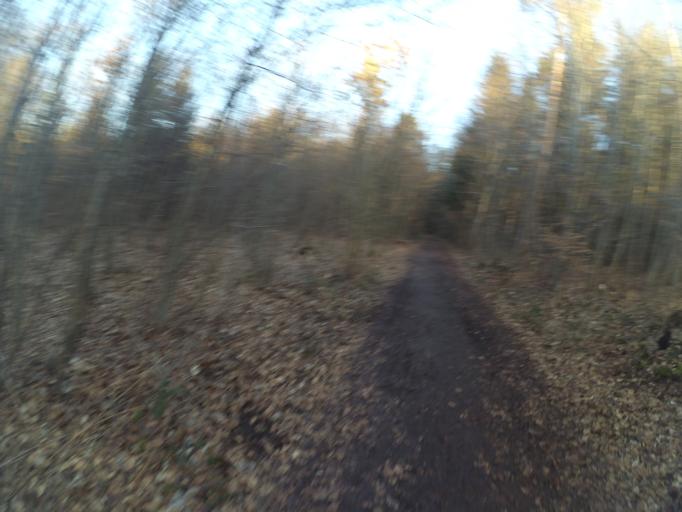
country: DE
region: Bavaria
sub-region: Swabia
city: Guenzburg
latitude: 48.4465
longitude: 10.3057
